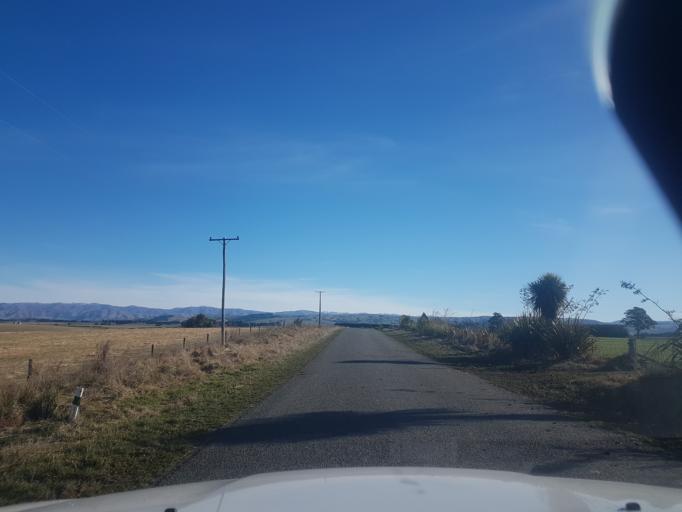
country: NZ
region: Canterbury
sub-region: Timaru District
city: Pleasant Point
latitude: -44.2545
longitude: 171.0352
